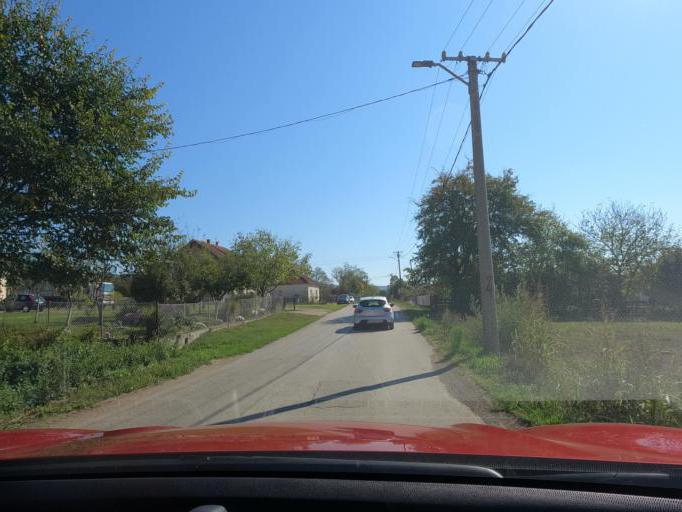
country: RS
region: Central Serbia
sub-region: Raski Okrug
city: Kraljevo
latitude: 43.7542
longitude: 20.6955
